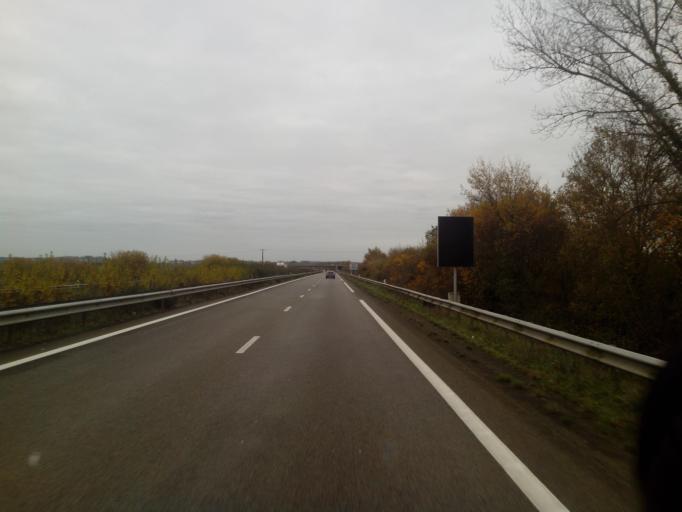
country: FR
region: Pays de la Loire
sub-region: Departement de la Loire-Atlantique
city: Le Pallet
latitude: 47.1562
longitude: -1.3263
